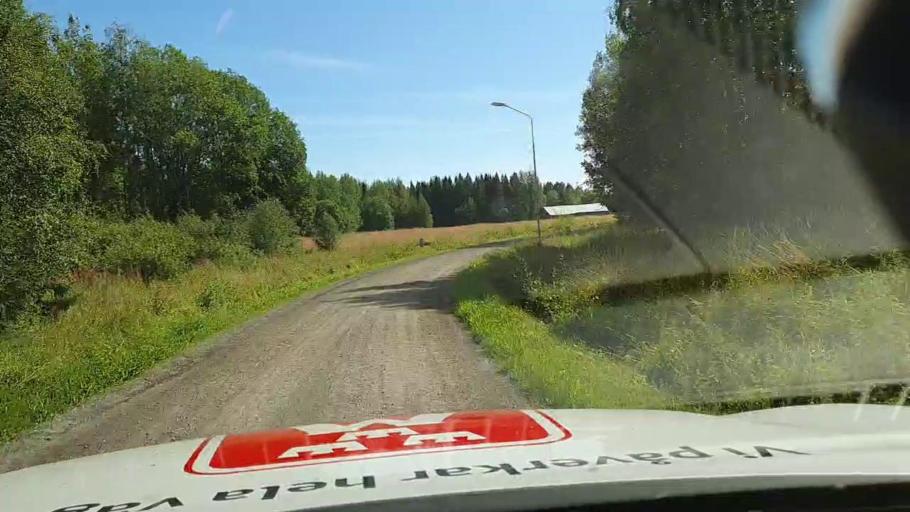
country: SE
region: Jaemtland
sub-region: Stroemsunds Kommun
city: Stroemsund
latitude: 63.7761
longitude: 15.3193
